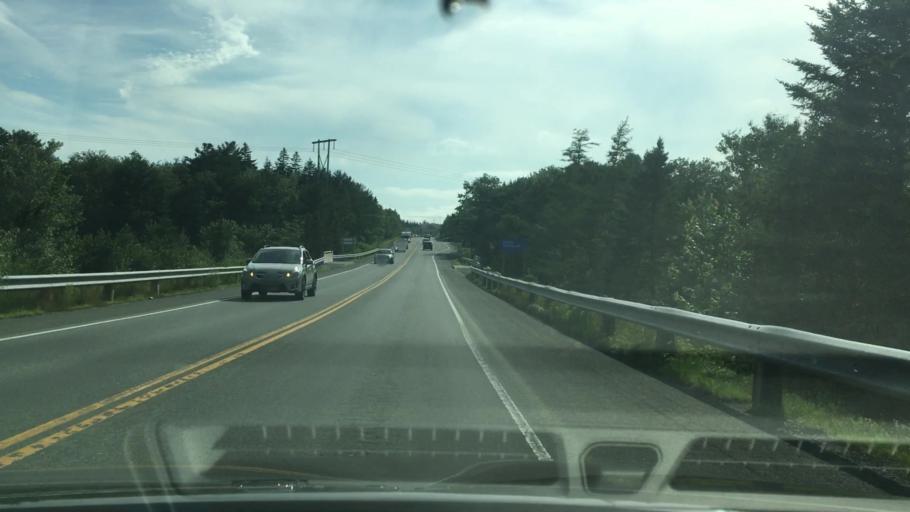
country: CA
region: Nova Scotia
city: Dartmouth
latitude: 44.7074
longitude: -63.8492
